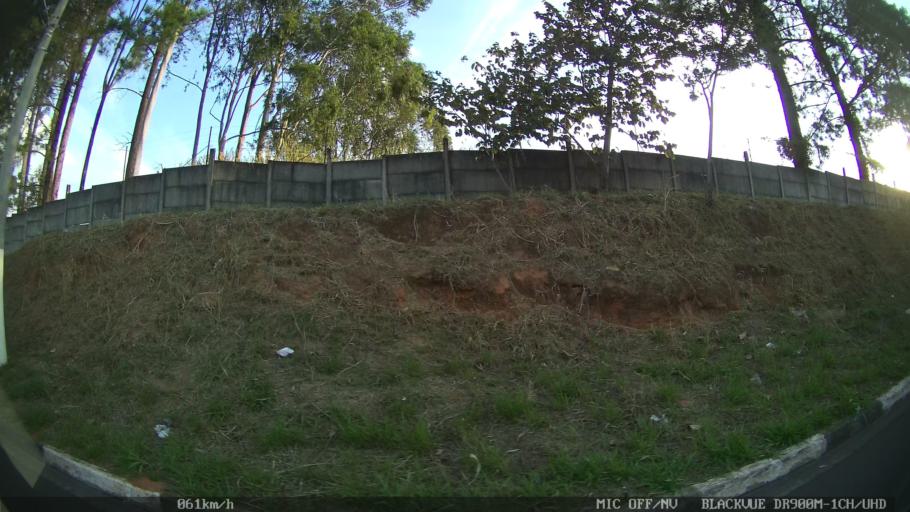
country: BR
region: Sao Paulo
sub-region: Hortolandia
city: Hortolandia
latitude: -22.8785
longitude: -47.1649
